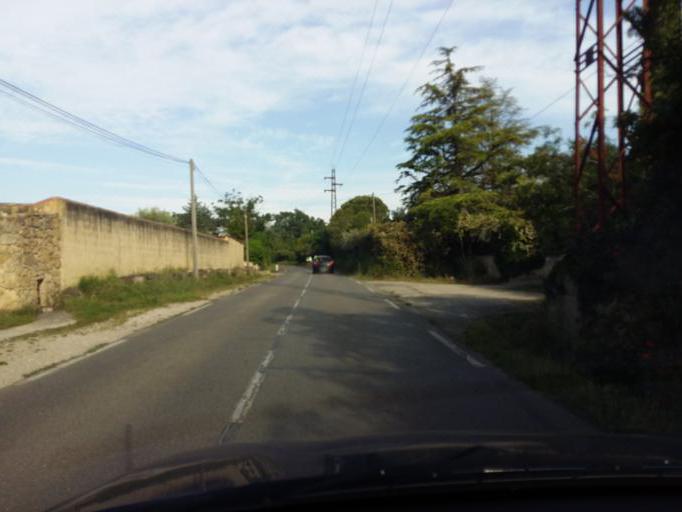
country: FR
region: Provence-Alpes-Cote d'Azur
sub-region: Departement des Bouches-du-Rhone
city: Pelissanne
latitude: 43.6340
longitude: 5.1364
